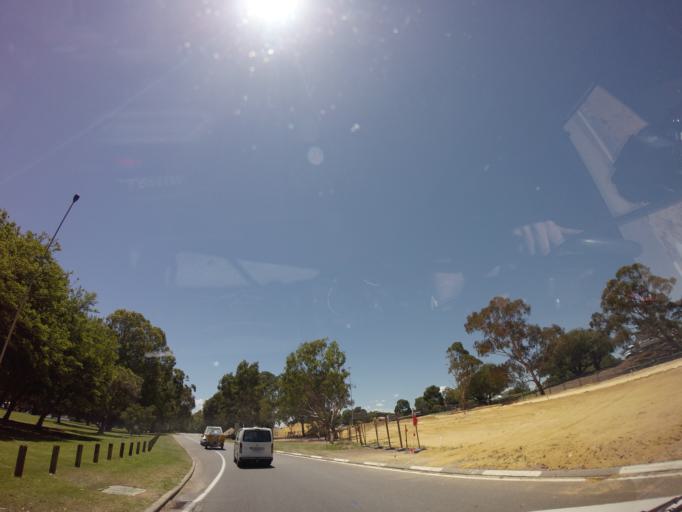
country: AU
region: Western Australia
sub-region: Belmont
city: Burswood
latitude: -31.9673
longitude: 115.8883
